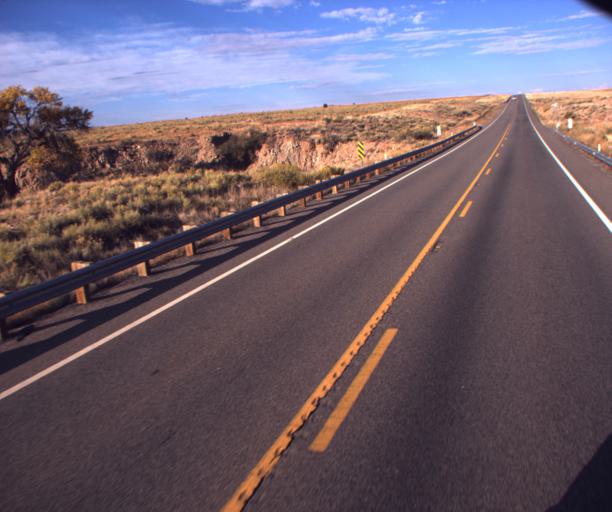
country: US
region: Arizona
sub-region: Apache County
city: Lukachukai
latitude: 36.9267
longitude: -109.1821
